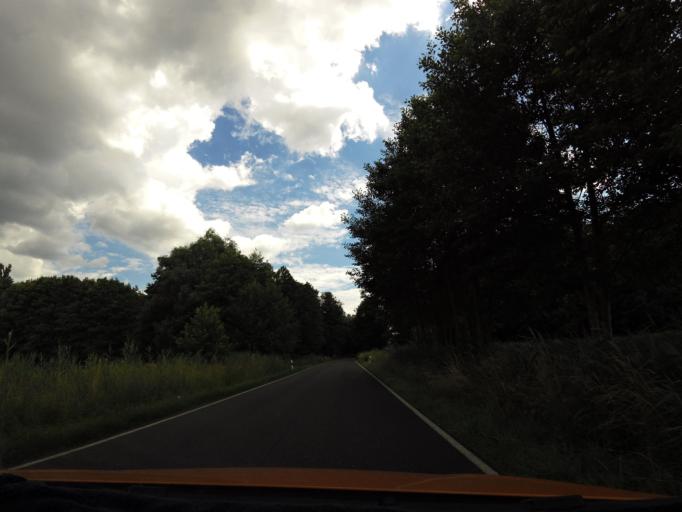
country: DE
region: Brandenburg
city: Munchehofe
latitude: 52.2467
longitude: 13.7994
